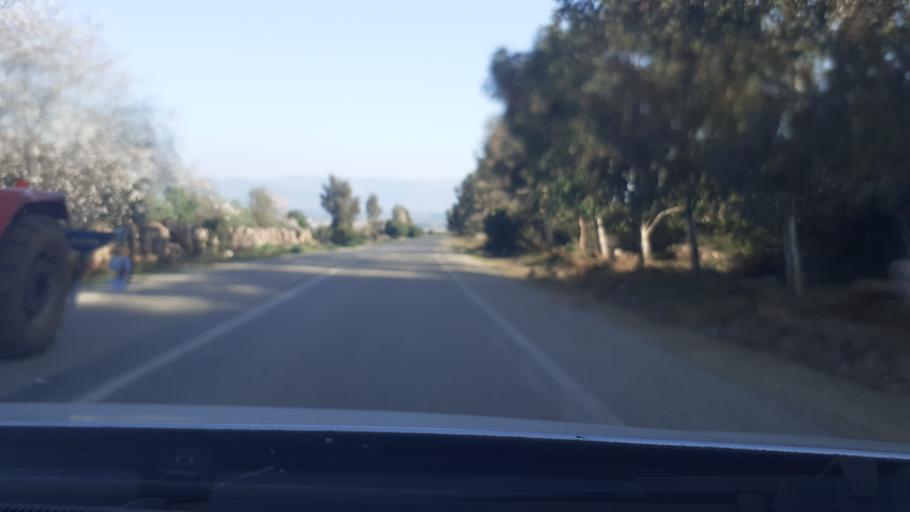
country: TR
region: Hatay
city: Aktepe
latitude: 36.7314
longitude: 36.4794
